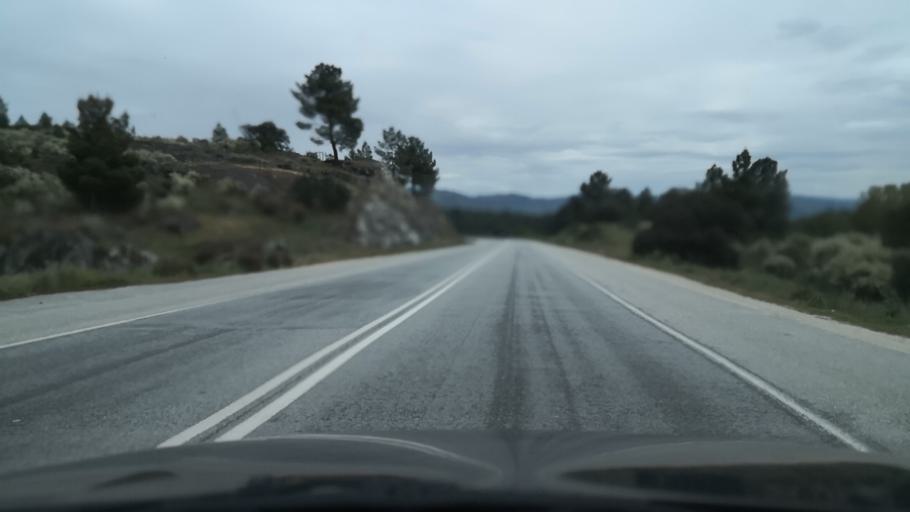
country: PT
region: Guarda
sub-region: Celorico da Beira
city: Celorico da Beira
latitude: 40.6381
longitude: -7.3237
